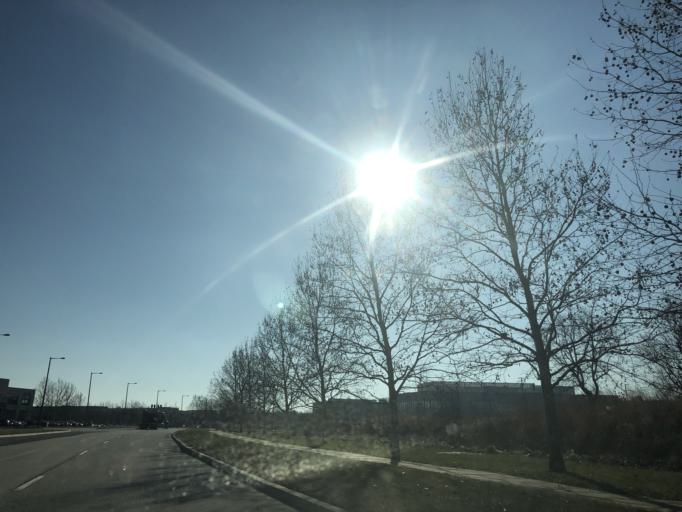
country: US
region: New Jersey
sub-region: Gloucester County
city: National Park
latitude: 39.8954
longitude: -75.1687
